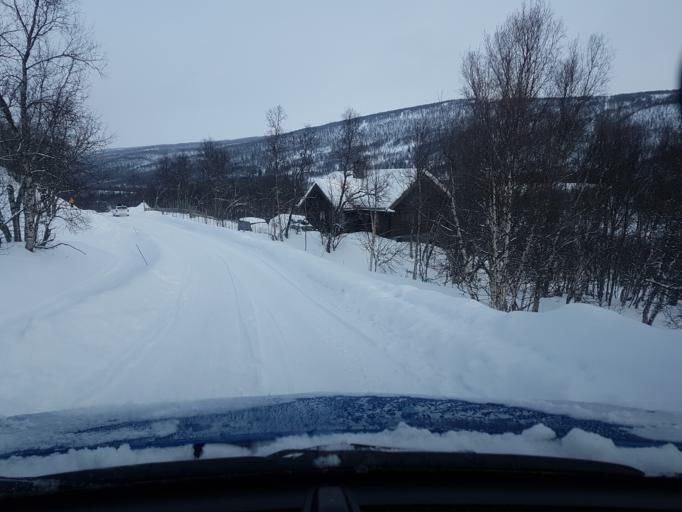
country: NO
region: Sor-Trondelag
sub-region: Tydal
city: Aas
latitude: 62.6919
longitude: 12.3990
